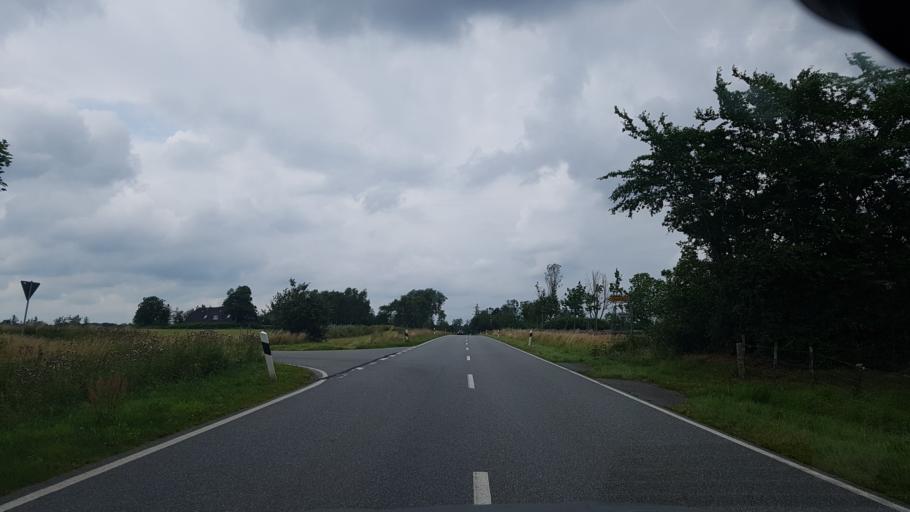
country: DE
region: Schleswig-Holstein
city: Osterby
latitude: 54.8147
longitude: 9.2290
